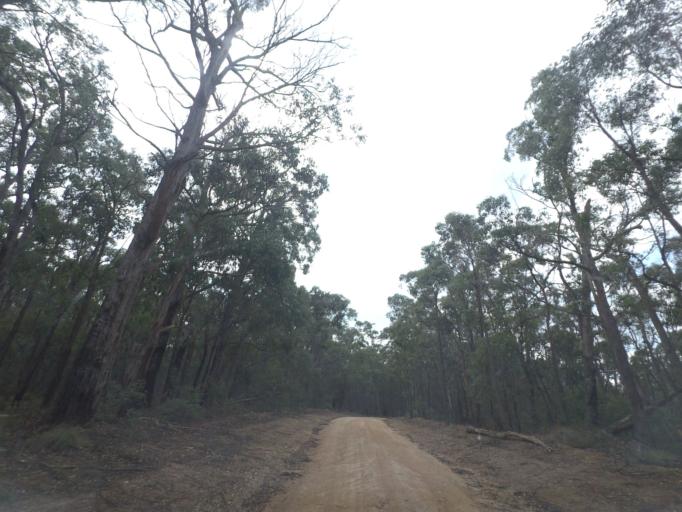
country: AU
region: Victoria
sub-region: Moorabool
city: Bacchus Marsh
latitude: -37.5267
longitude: 144.4357
